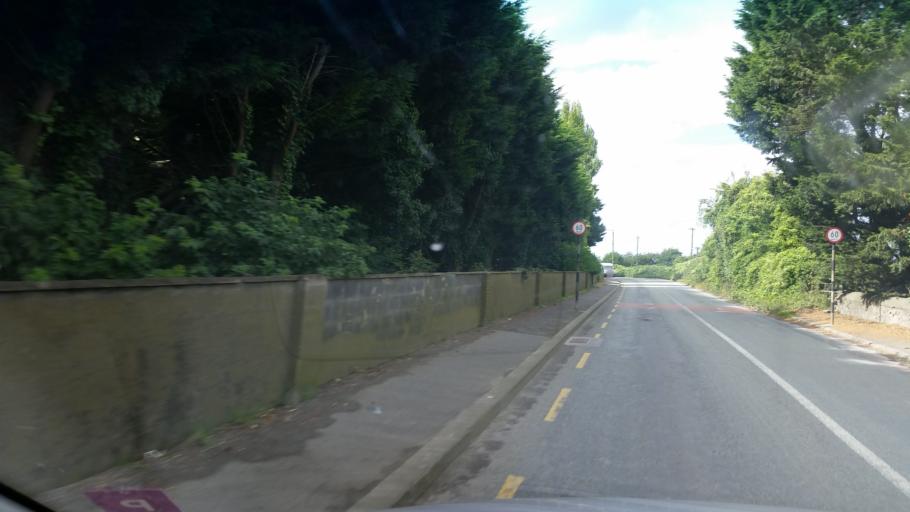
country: IE
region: Leinster
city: Kinsealy-Drinan
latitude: 53.4369
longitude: -6.1860
